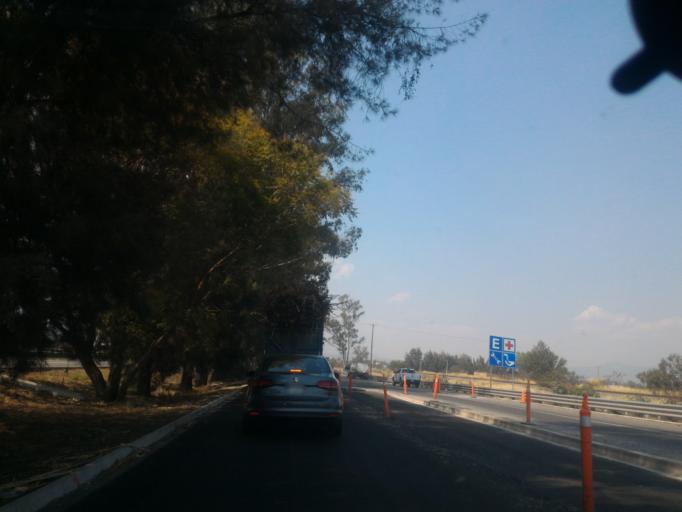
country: MX
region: Jalisco
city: Ciudad Guzman
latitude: 19.7040
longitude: -103.4991
